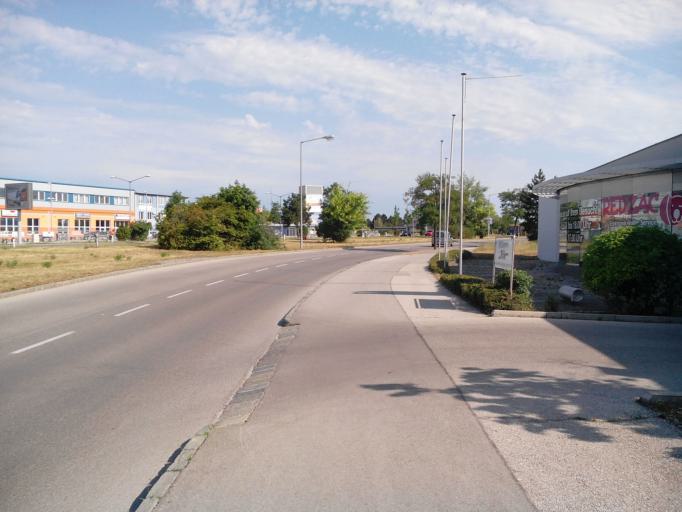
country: AT
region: Lower Austria
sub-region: Politischer Bezirk Wiener Neustadt
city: Theresienfeld
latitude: 47.8355
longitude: 16.2457
